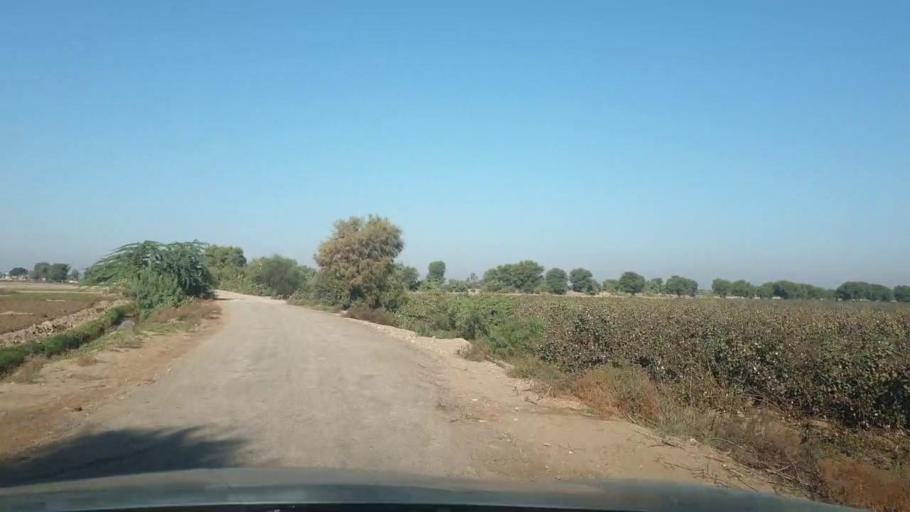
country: PK
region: Sindh
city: Bhan
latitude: 26.5499
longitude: 67.6658
